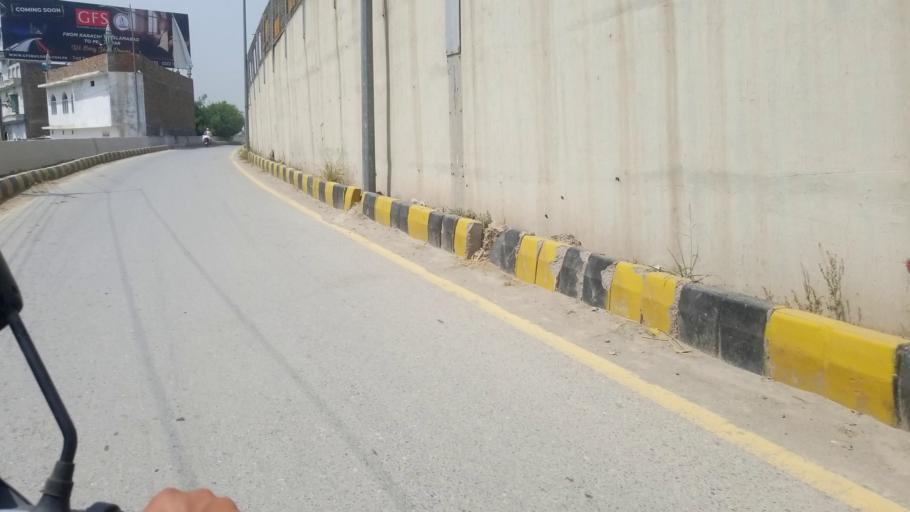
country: PK
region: Khyber Pakhtunkhwa
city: Peshawar
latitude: 34.0303
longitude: 71.5530
